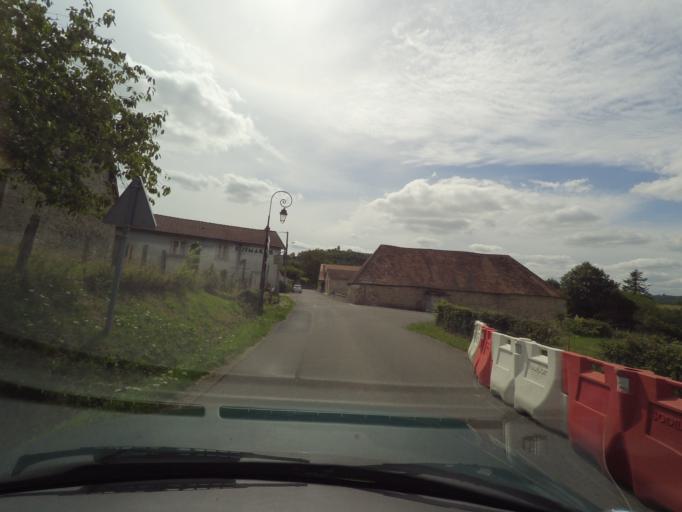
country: FR
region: Limousin
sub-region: Departement de la Haute-Vienne
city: Ladignac-le-Long
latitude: 45.6489
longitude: 1.1230
